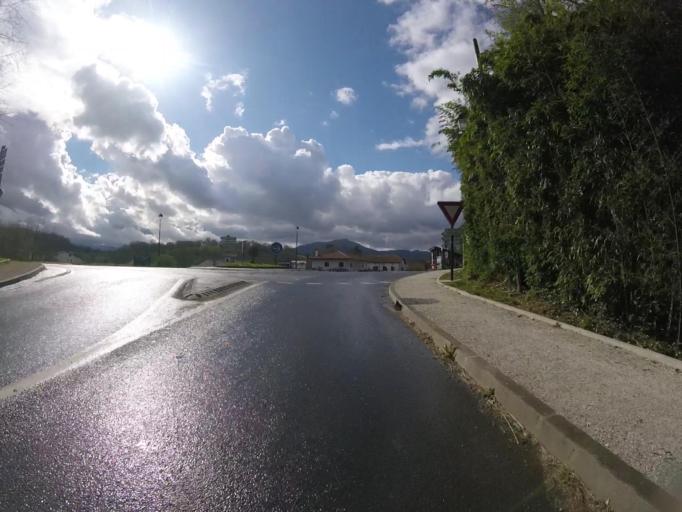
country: FR
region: Aquitaine
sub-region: Departement des Pyrenees-Atlantiques
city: Sare
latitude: 43.3098
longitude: -1.5723
